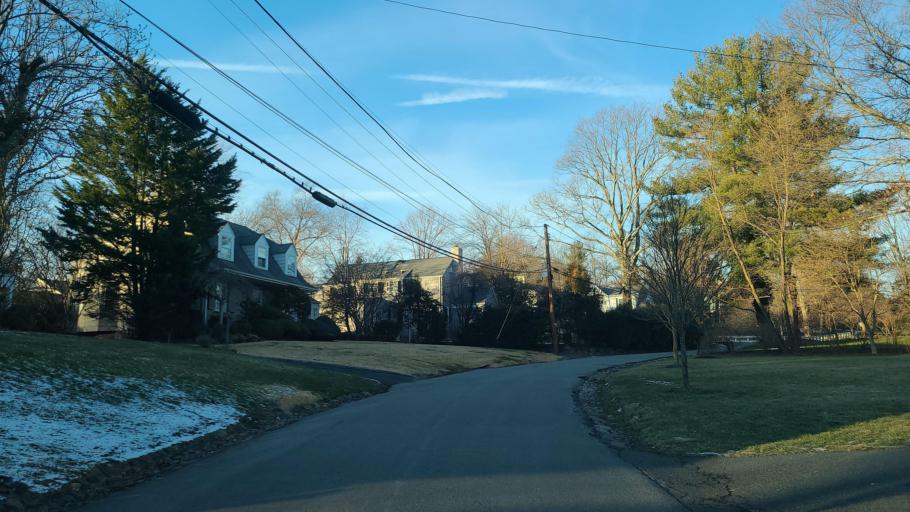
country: US
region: New Jersey
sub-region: Essex County
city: Short Hills
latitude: 40.7271
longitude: -74.3288
